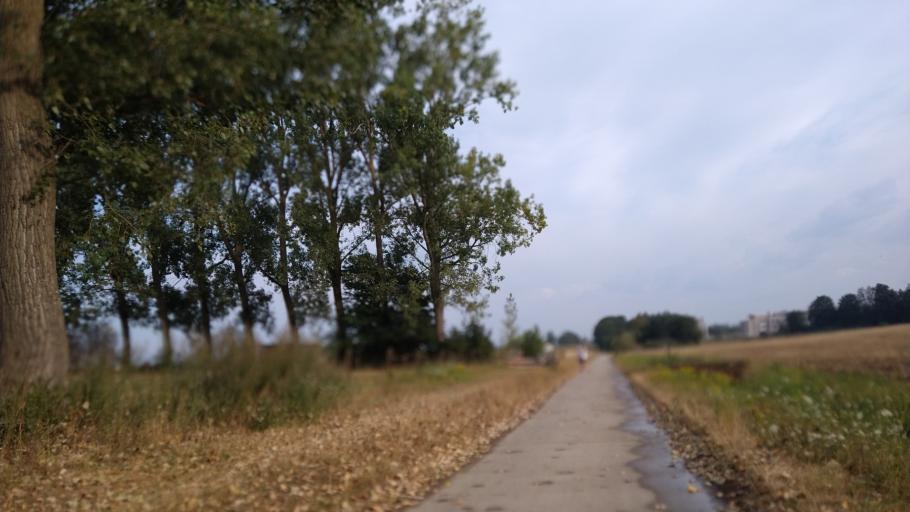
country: BE
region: Flanders
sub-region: Provincie Vlaams-Brabant
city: Wezembeek-Oppem
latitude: 50.8486
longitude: 4.5162
